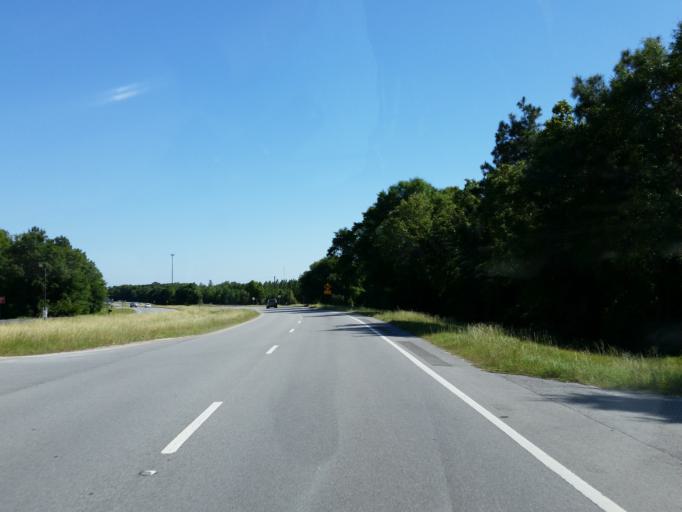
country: US
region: Georgia
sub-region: Lowndes County
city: Valdosta
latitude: 30.6996
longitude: -83.2109
